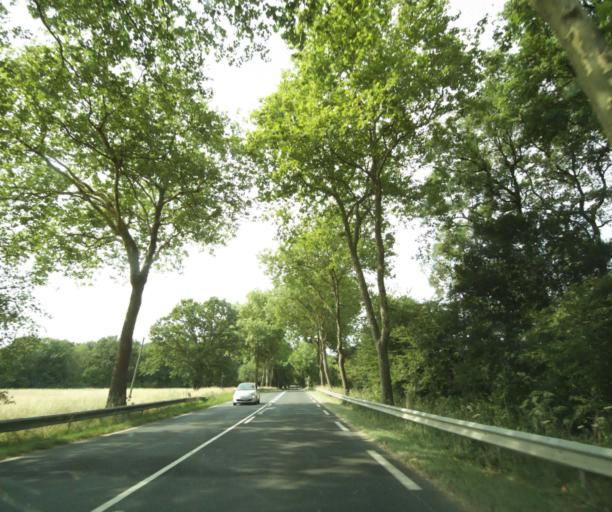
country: FR
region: Centre
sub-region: Departement d'Indre-et-Loire
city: Neuille-Pont-Pierre
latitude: 47.5841
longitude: 0.5402
